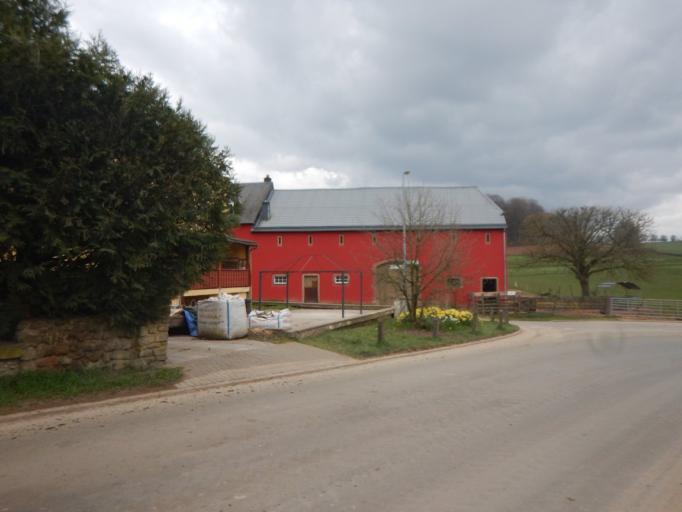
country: LU
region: Diekirch
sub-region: Canton de Redange
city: Ell
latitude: 49.7874
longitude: 5.8387
